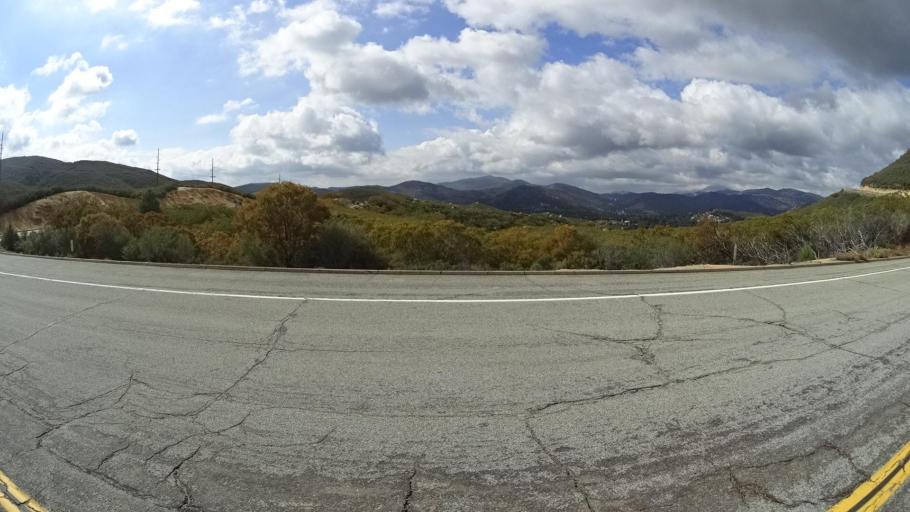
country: US
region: California
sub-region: San Diego County
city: Pine Valley
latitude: 32.8134
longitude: -116.5090
